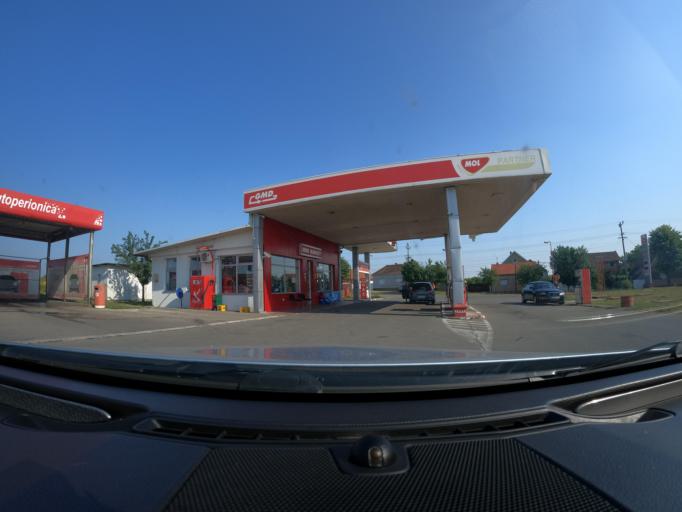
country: RS
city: Putinci
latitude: 44.9920
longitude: 19.9837
